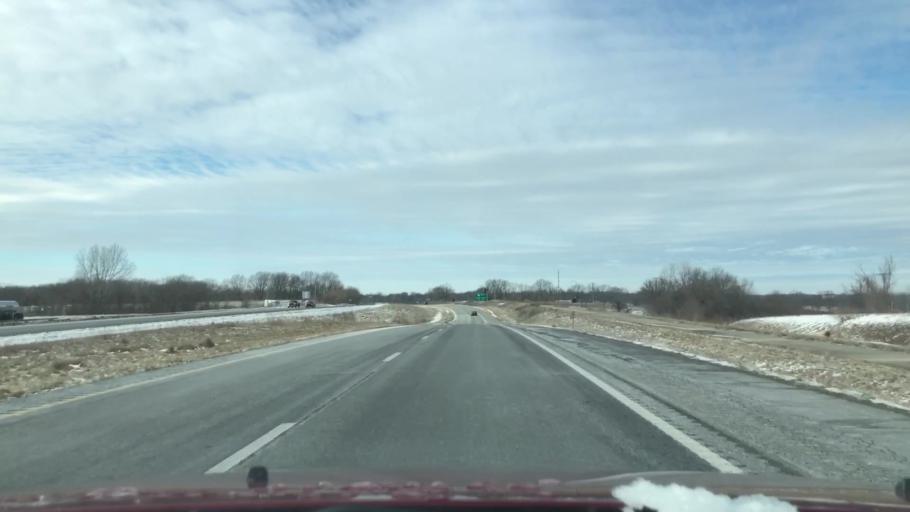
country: US
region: Missouri
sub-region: Jackson County
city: Lone Jack
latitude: 38.8710
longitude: -94.1483
